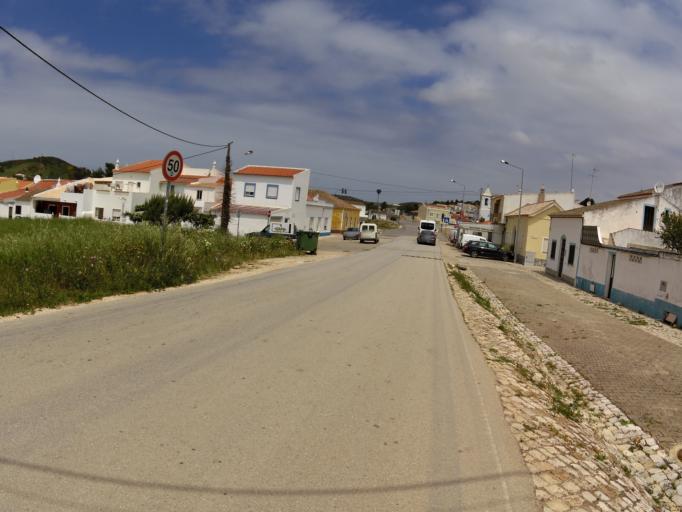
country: PT
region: Faro
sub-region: Vila do Bispo
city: Vila do Bispo
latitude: 37.0813
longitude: -8.8896
